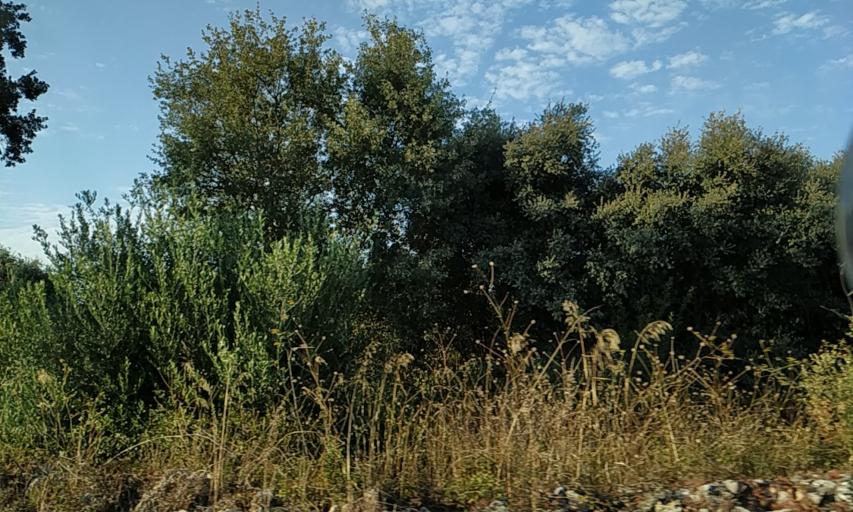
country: PT
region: Santarem
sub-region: Alcanena
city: Alcanena
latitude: 39.4535
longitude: -8.6268
